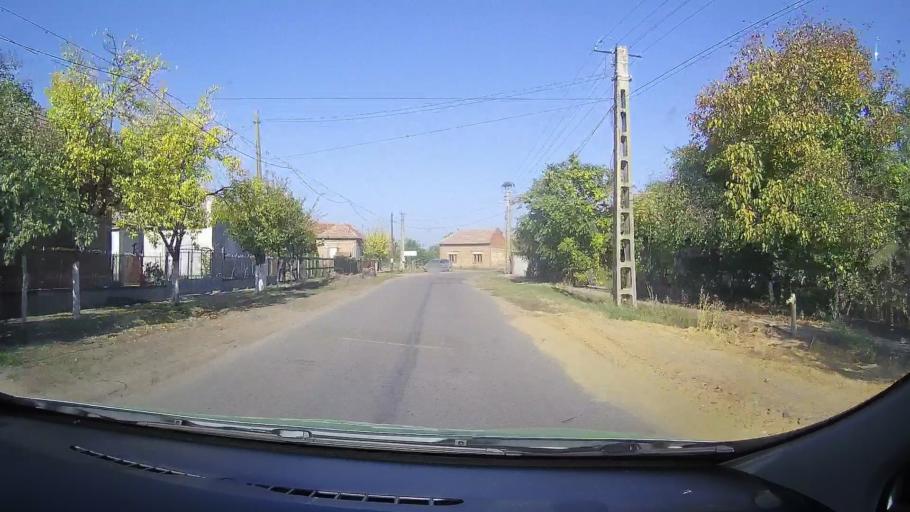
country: RO
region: Satu Mare
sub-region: Comuna Ciumesti
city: Ciumesti
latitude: 47.6555
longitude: 22.3339
